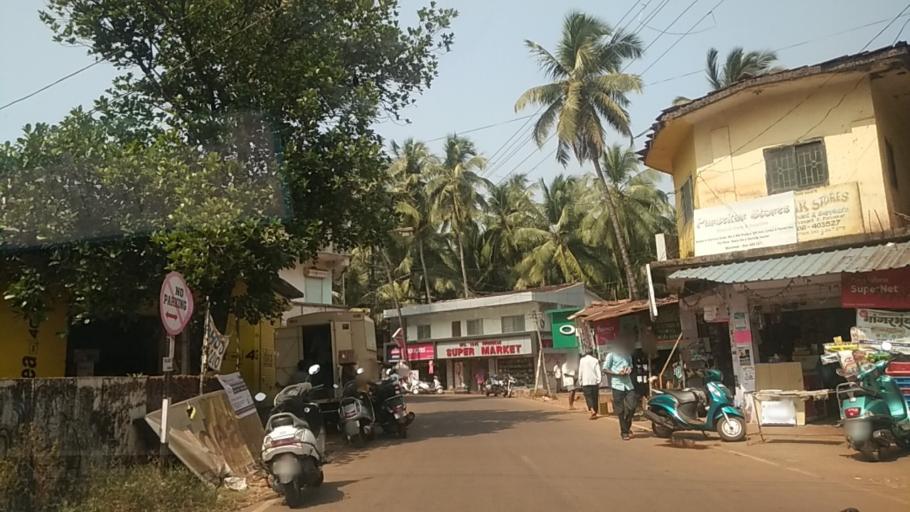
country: IN
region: Goa
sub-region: North Goa
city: Arambol
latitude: 15.6668
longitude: 73.7219
